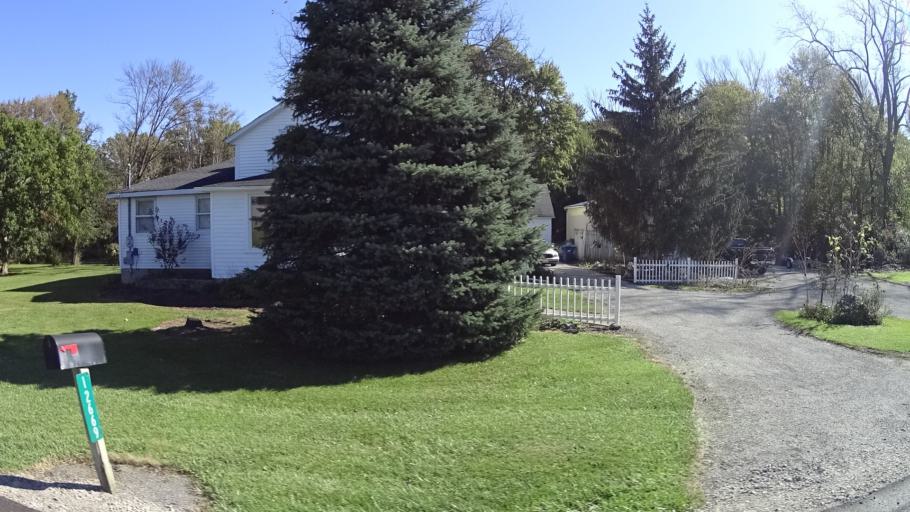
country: US
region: Ohio
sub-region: Lorain County
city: Oberlin
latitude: 41.2998
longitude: -82.1970
